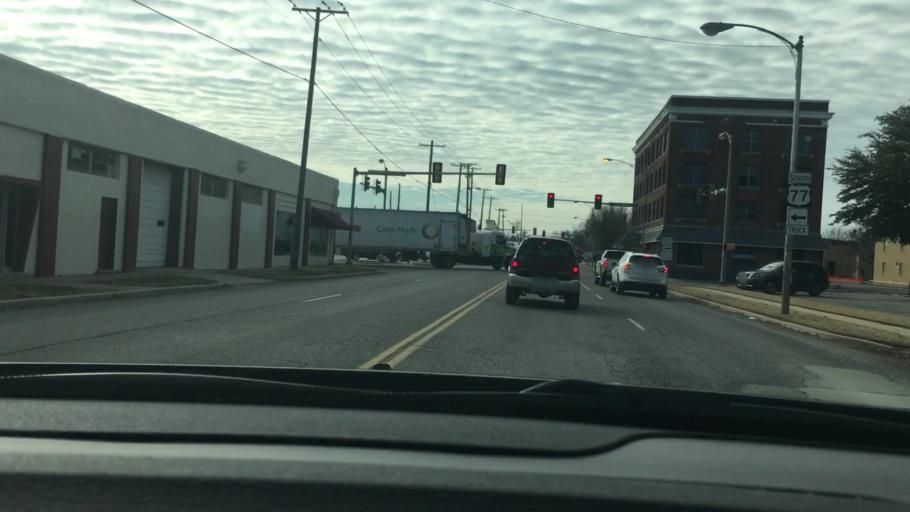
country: US
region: Oklahoma
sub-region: Garvin County
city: Pauls Valley
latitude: 34.7417
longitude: -97.2199
